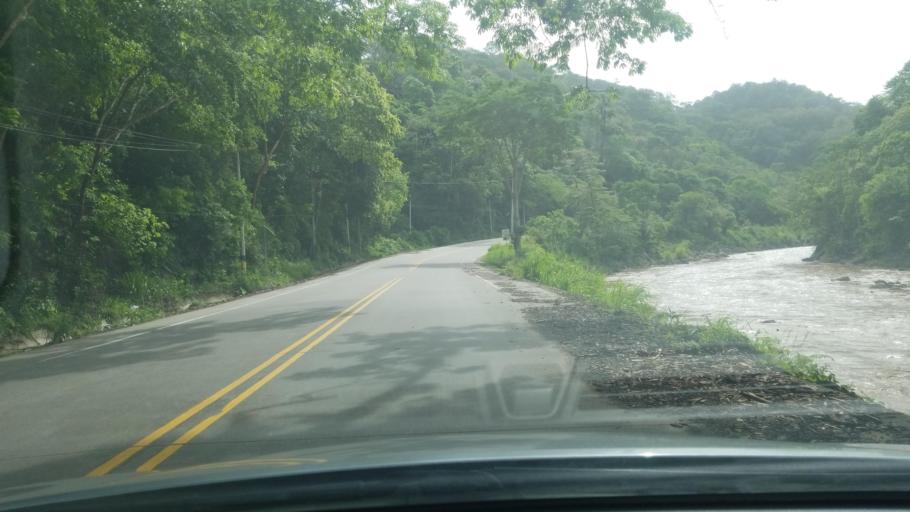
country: HN
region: Copan
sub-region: Santa Rita
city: Santa Rita, Copan
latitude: 14.8705
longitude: -89.0805
